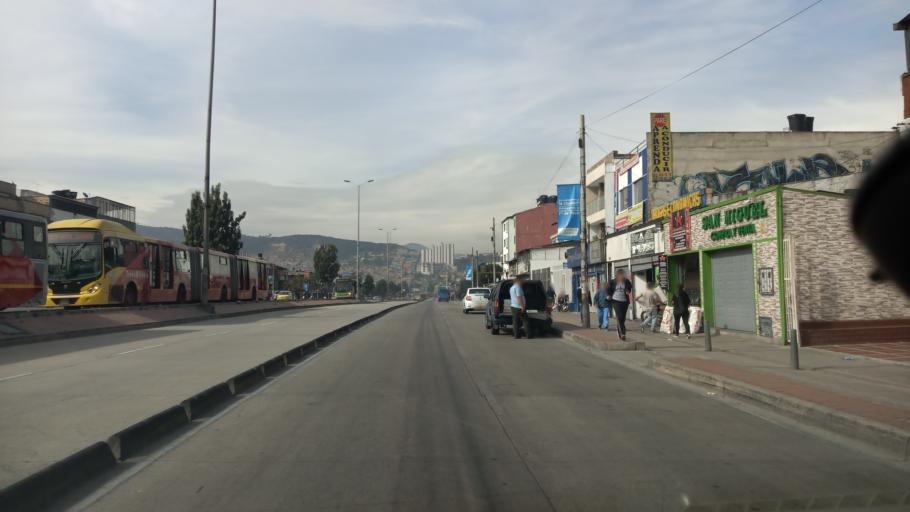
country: CO
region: Bogota D.C.
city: Bogota
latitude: 4.5755
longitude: -74.0950
